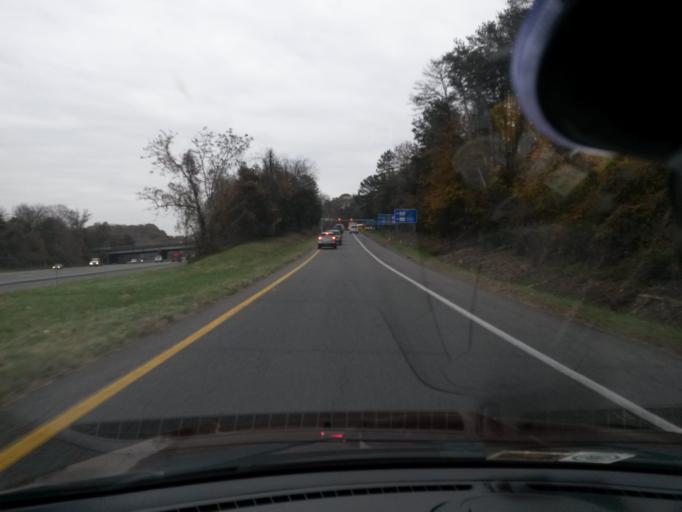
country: US
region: Virginia
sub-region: City of Charlottesville
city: Charlottesville
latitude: 38.0080
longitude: -78.5123
